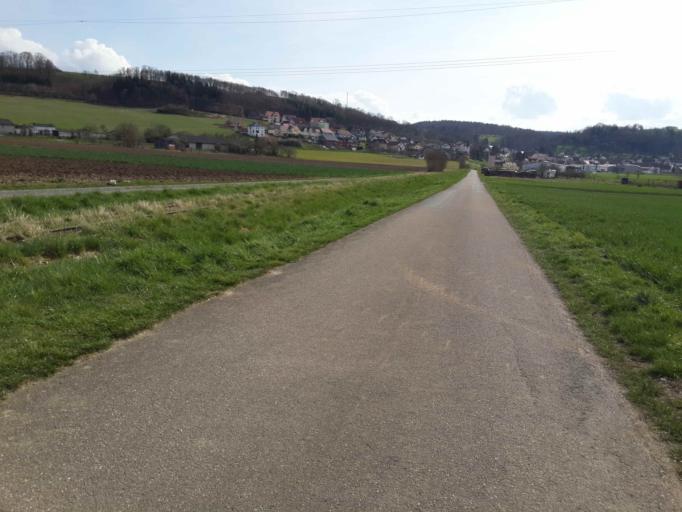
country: DE
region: Baden-Wuerttemberg
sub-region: Regierungsbezirk Stuttgart
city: Weissbach
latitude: 49.3509
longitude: 9.5686
